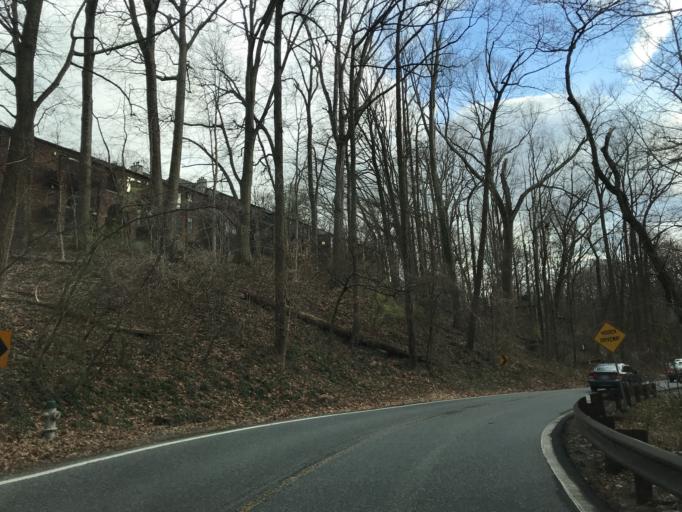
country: US
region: Maryland
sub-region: Montgomery County
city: Takoma Park
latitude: 38.9931
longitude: -77.0051
